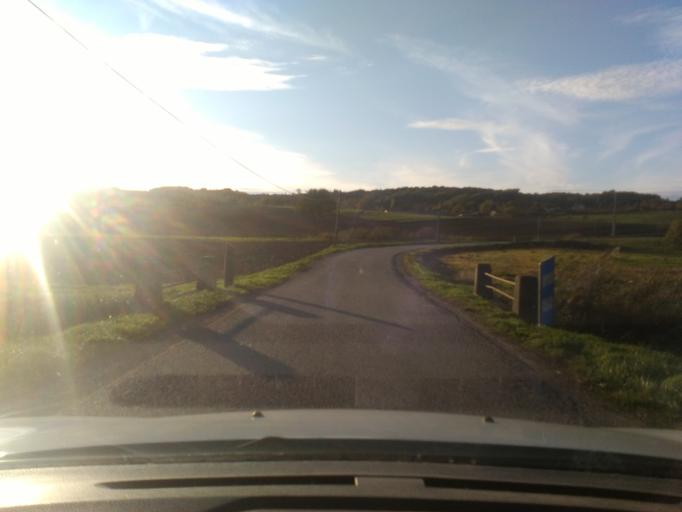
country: FR
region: Lorraine
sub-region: Departement des Vosges
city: Charmes
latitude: 48.3341
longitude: 6.2849
